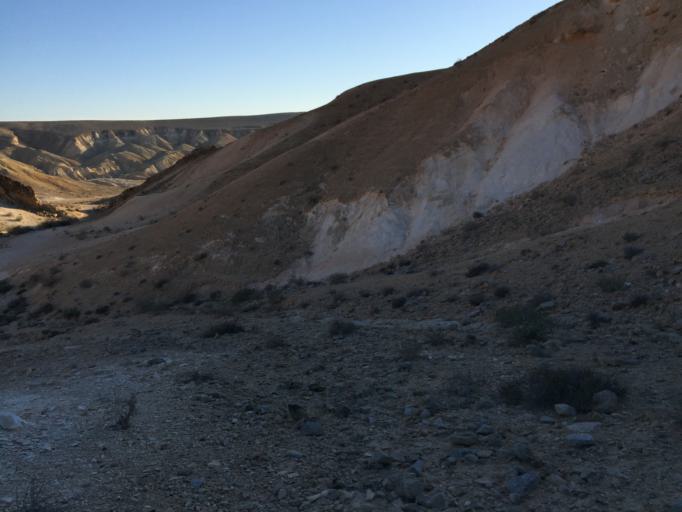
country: IL
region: Southern District
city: Midreshet Ben-Gurion
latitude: 30.8467
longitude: 34.7557
